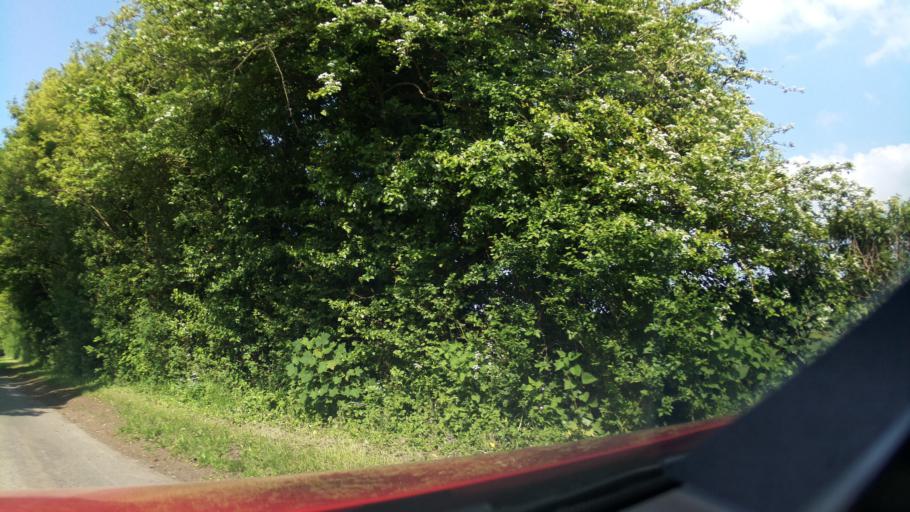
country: GB
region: England
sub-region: Wiltshire
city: Luckington
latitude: 51.5811
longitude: -2.2703
